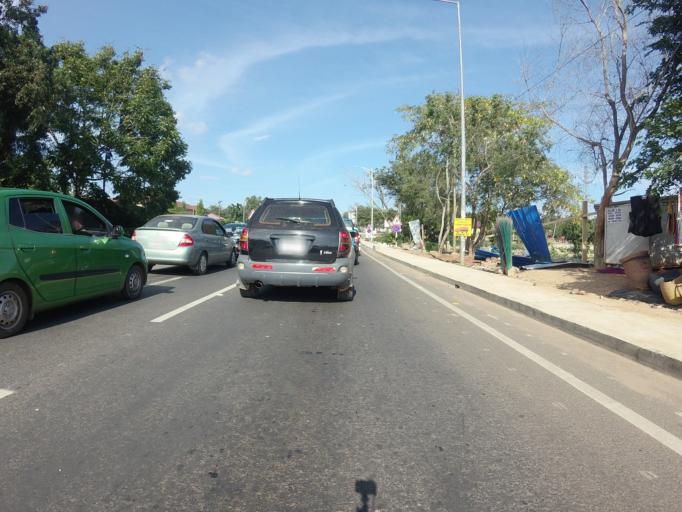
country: GH
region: Greater Accra
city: Medina Estates
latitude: 5.6304
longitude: -0.1579
